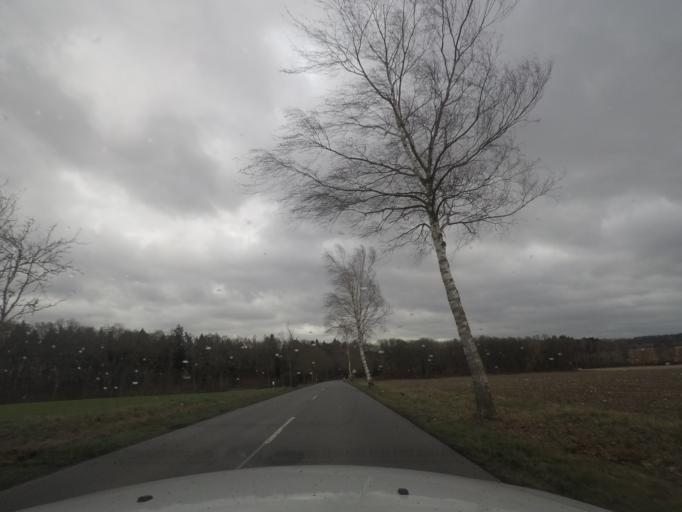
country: DE
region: Lower Saxony
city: Emmendorf
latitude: 53.0292
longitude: 10.6049
